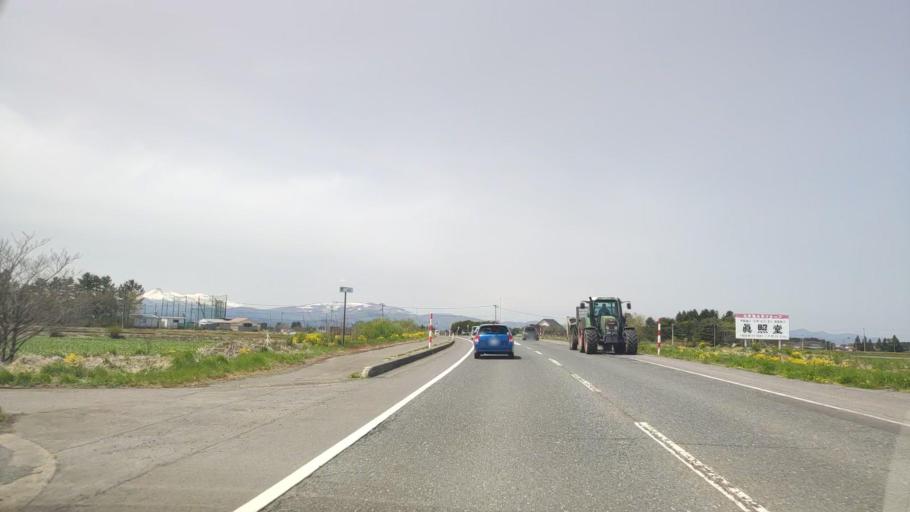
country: JP
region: Aomori
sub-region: Misawa Shi
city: Inuotose
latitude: 40.6377
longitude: 141.2403
